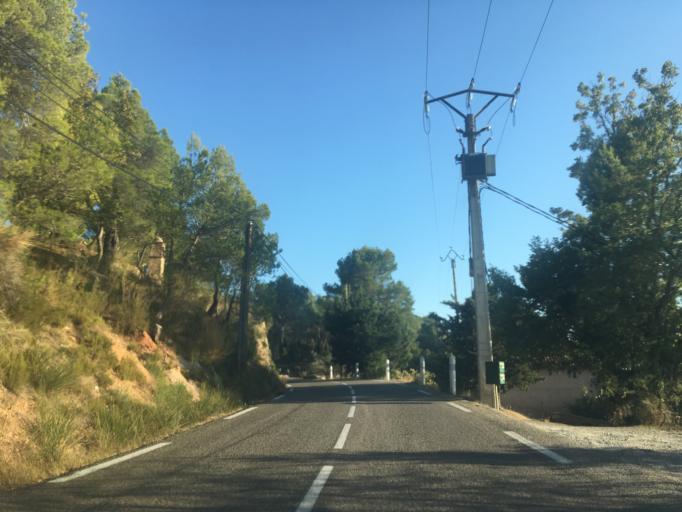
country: FR
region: Provence-Alpes-Cote d'Azur
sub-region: Departement du Var
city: Villecroze
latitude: 43.5782
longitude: 6.2825
